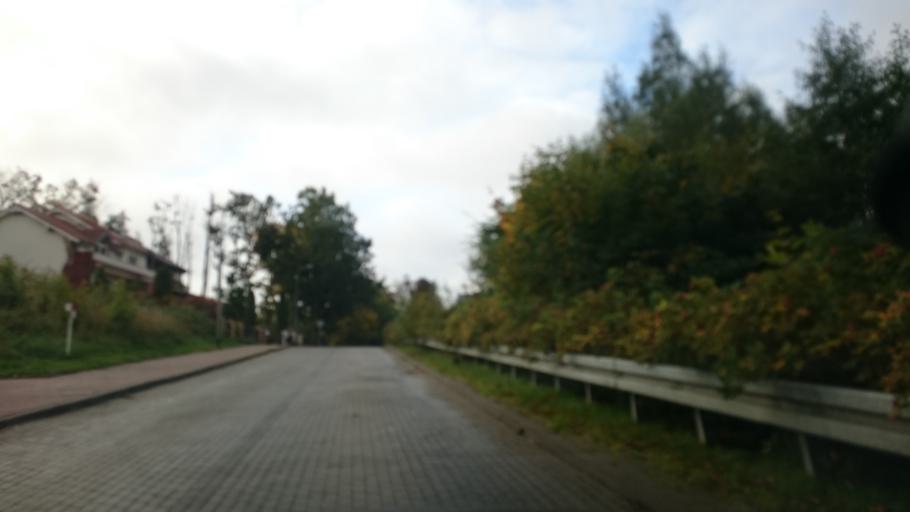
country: PL
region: Pomeranian Voivodeship
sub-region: Gdynia
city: Wielki Kack
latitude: 54.4656
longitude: 18.4935
